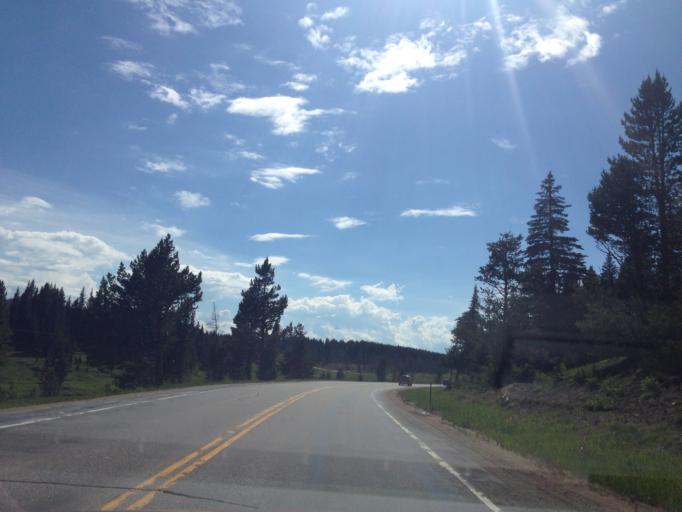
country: US
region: Colorado
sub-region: Routt County
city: Steamboat Springs
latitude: 40.3890
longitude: -106.6527
